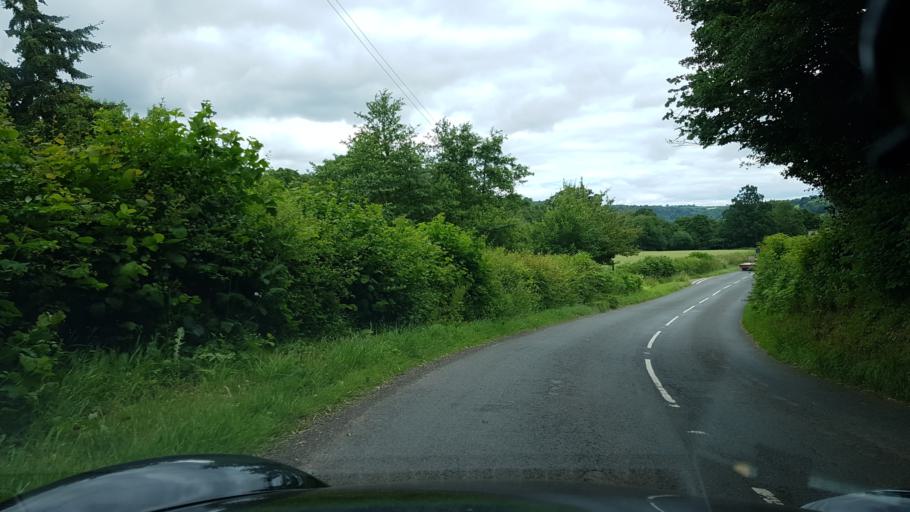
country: GB
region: England
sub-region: Herefordshire
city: Llanrothal
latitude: 51.8765
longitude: -2.8163
